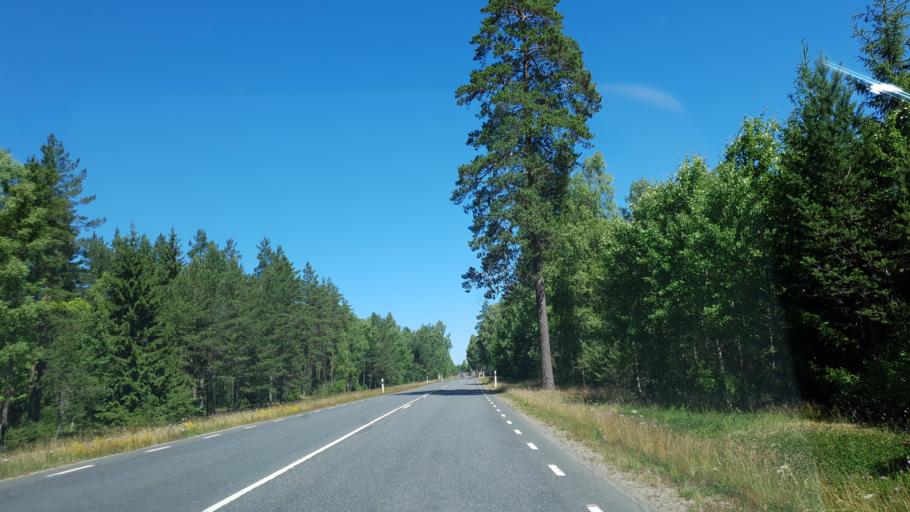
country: SE
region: Joenkoeping
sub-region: Vaggeryds Kommun
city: Vaggeryd
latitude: 57.5307
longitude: 14.1383
